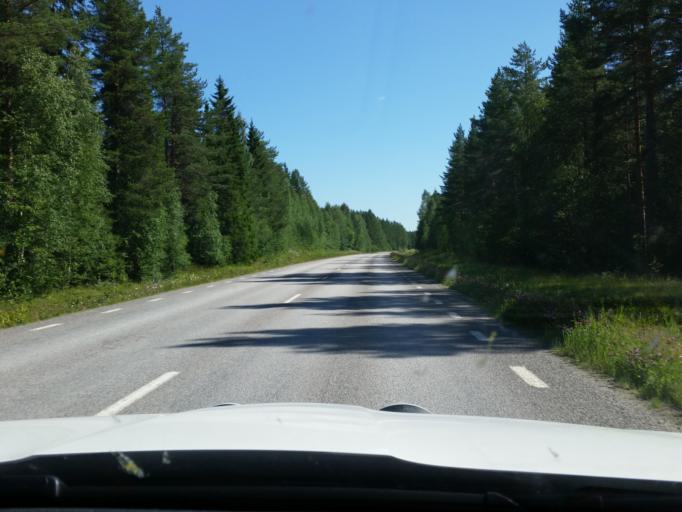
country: SE
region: Norrbotten
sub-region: Alvsbyns Kommun
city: AElvsbyn
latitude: 65.6790
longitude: 20.8161
